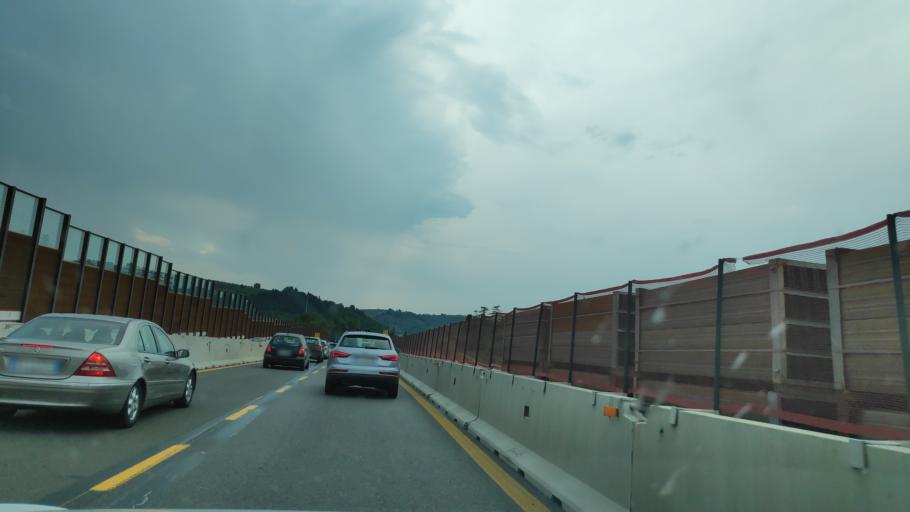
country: IT
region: Tuscany
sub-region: Province of Florence
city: Antella
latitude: 43.7295
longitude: 11.3280
